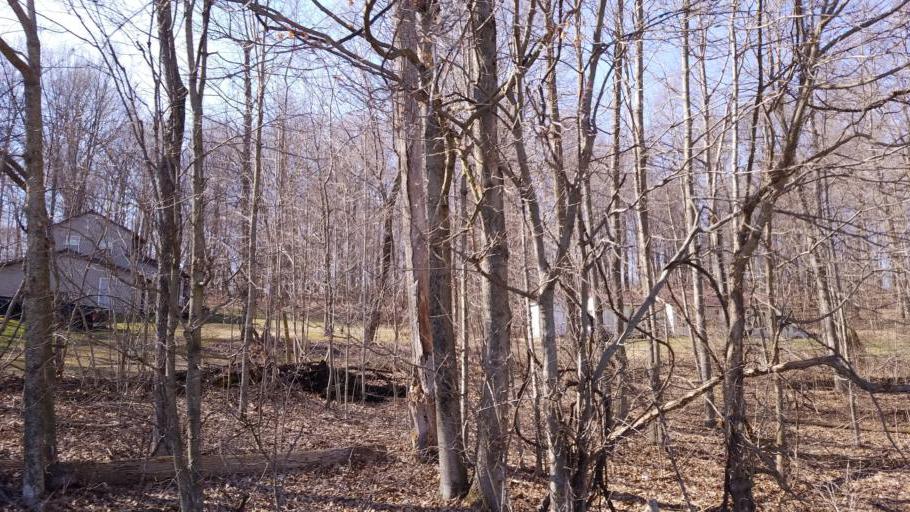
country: US
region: Ohio
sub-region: Knox County
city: Fredericktown
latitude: 40.5065
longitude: -82.4464
